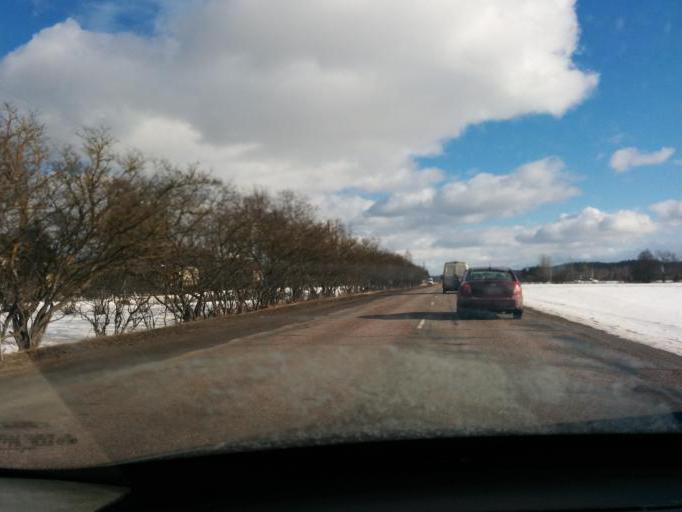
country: LV
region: Cesvaine
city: Cesvaine
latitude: 57.2395
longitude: 26.3959
